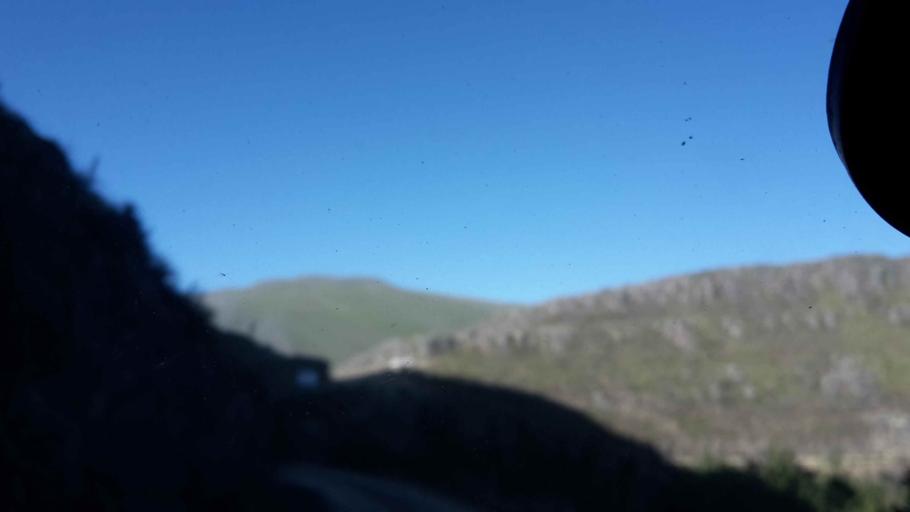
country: BO
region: Cochabamba
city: Arani
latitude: -17.7269
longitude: -65.6332
